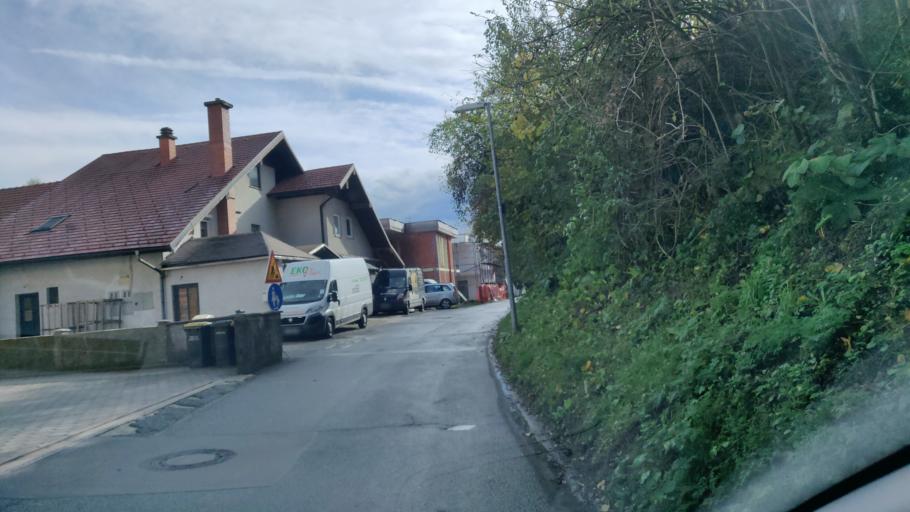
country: SI
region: Trzin
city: Trzin
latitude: 46.1330
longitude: 14.5607
